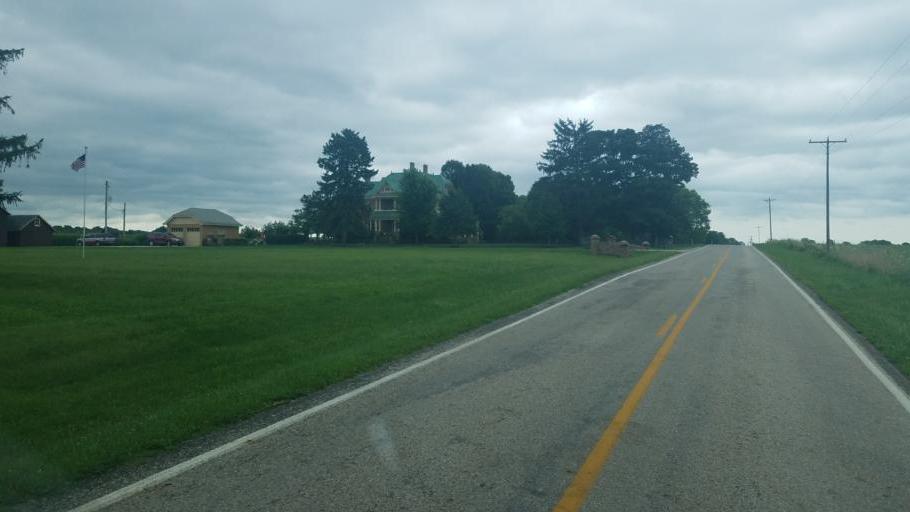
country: US
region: Ohio
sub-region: Pickaway County
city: Circleville
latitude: 39.6436
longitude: -82.9854
